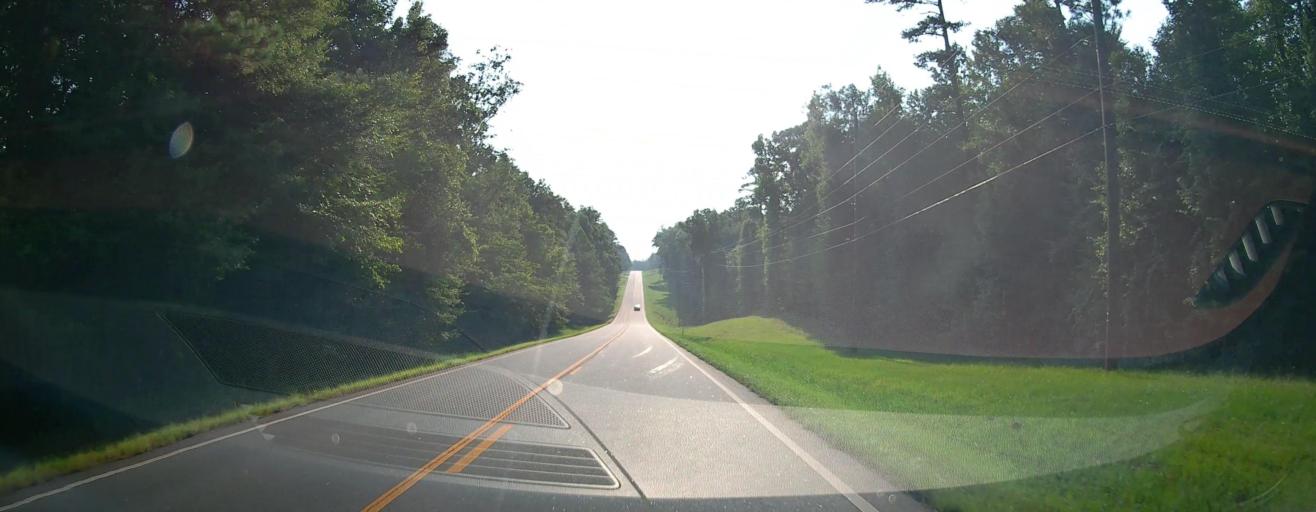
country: US
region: Georgia
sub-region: Bibb County
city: West Point
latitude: 32.8653
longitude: -83.8227
